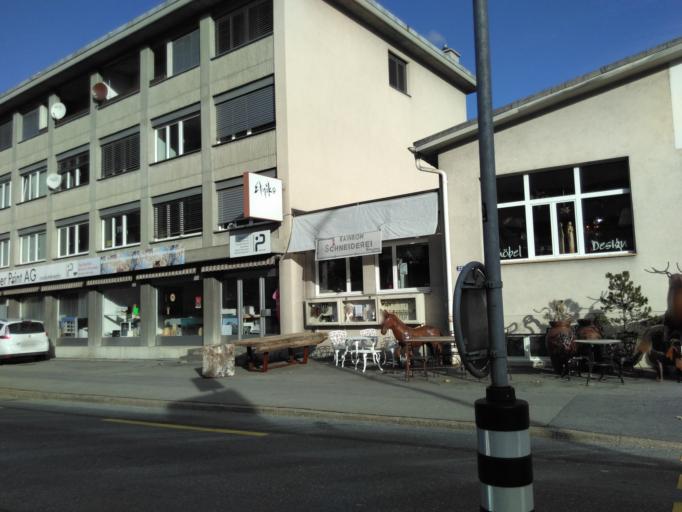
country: CH
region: Grisons
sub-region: Plessur District
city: Chur
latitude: 46.8516
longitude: 9.5133
